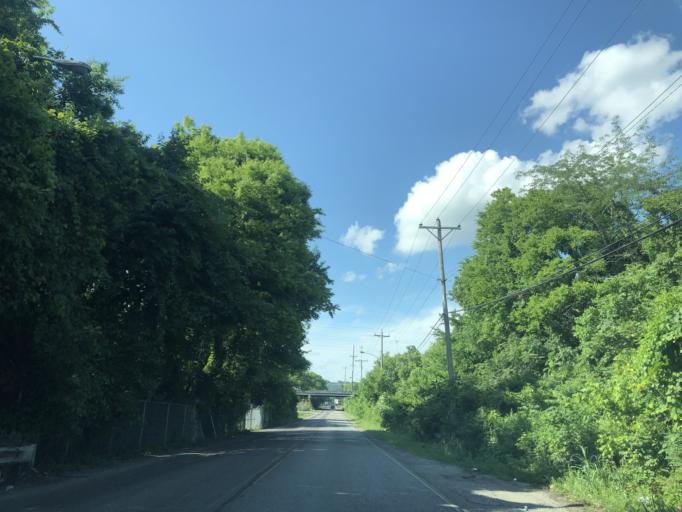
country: US
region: Tennessee
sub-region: Davidson County
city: Nashville
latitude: 36.2320
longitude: -86.8038
